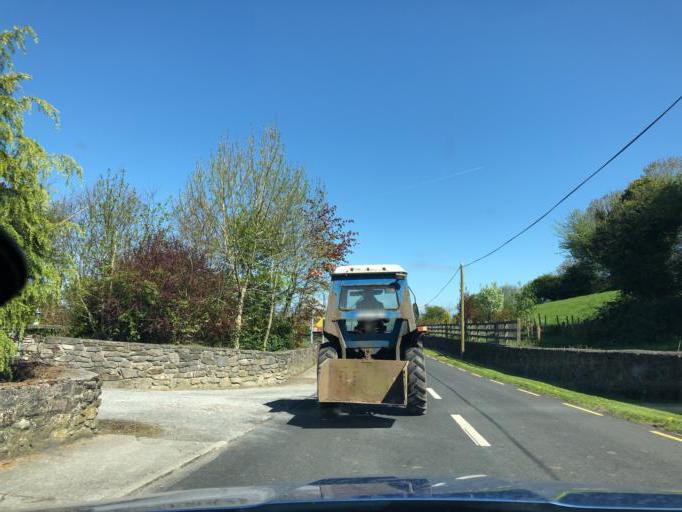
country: IE
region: Connaught
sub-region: County Galway
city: Portumna
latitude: 53.1479
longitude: -8.3720
